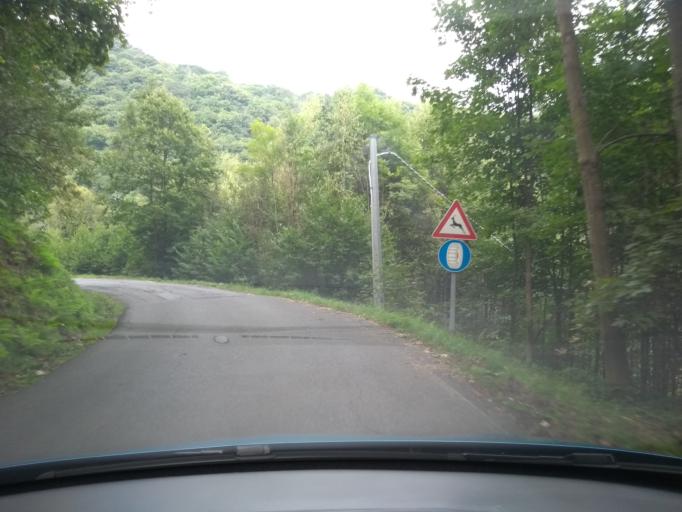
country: IT
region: Piedmont
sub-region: Provincia di Torino
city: Corio
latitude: 45.3318
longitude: 7.5150
